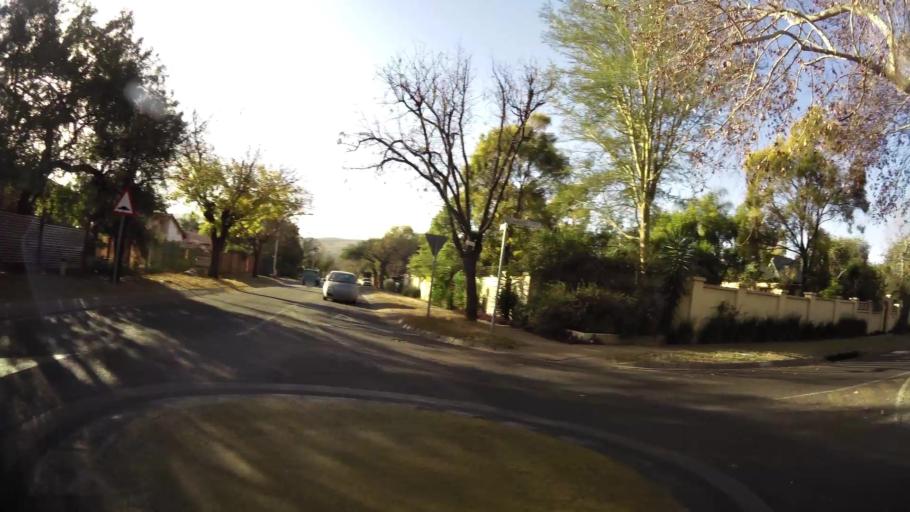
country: ZA
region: Gauteng
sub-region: City of Tshwane Metropolitan Municipality
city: Pretoria
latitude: -25.7117
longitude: 28.2061
